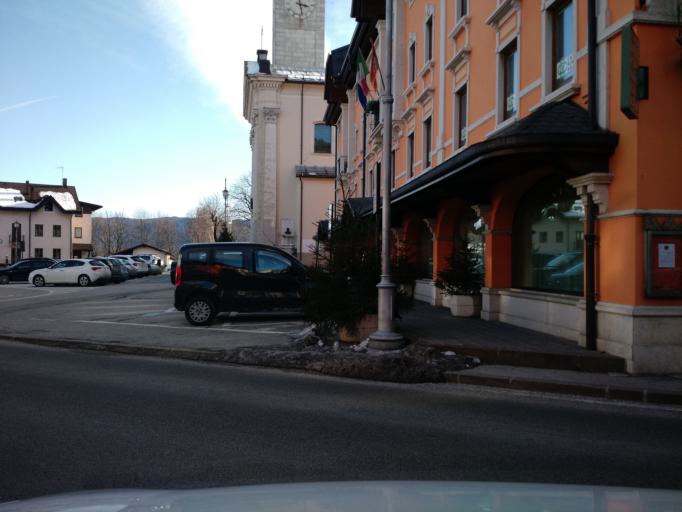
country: IT
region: Veneto
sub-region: Provincia di Vicenza
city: Roana
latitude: 45.8756
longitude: 11.4626
